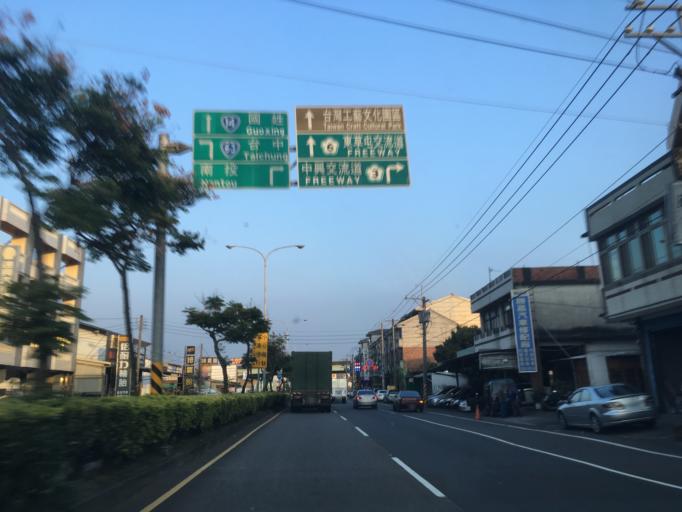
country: TW
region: Taiwan
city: Zhongxing New Village
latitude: 23.9988
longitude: 120.6605
